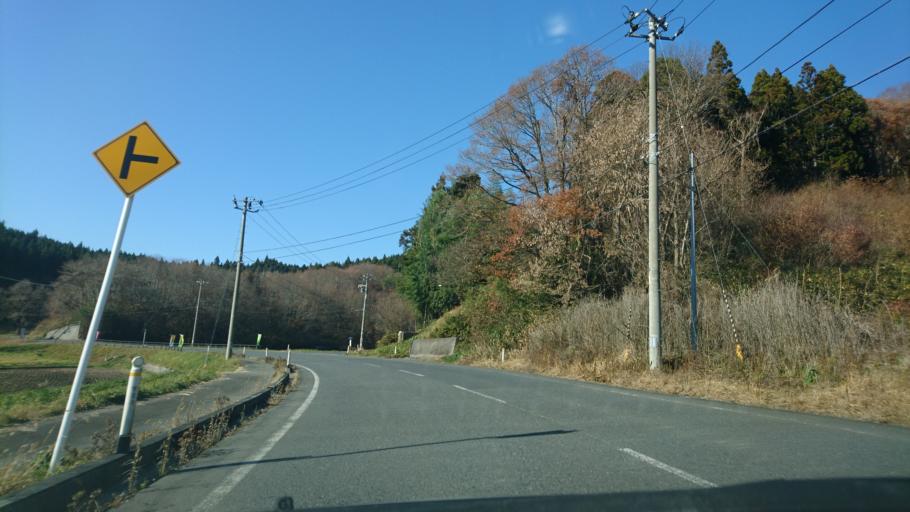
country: JP
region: Iwate
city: Ichinoseki
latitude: 38.9038
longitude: 141.4163
